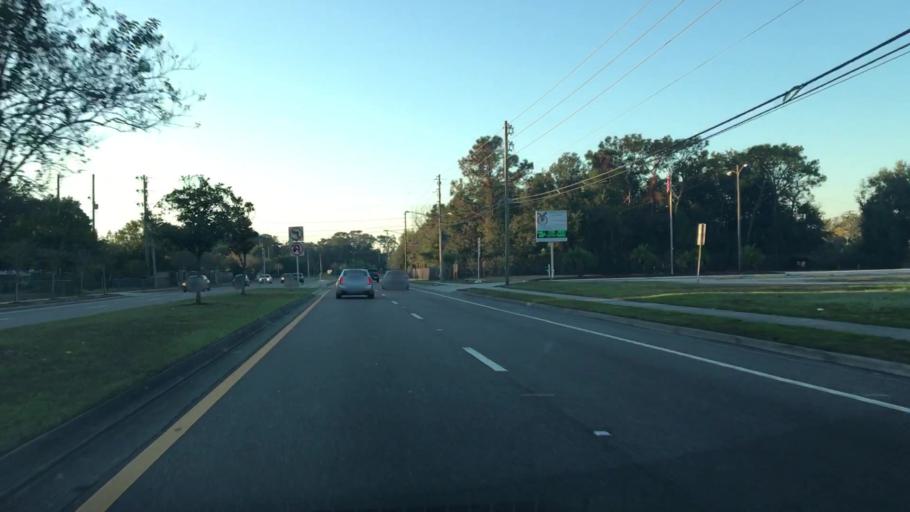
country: US
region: Florida
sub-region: Orange County
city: Azalea Park
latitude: 28.5254
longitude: -81.2857
